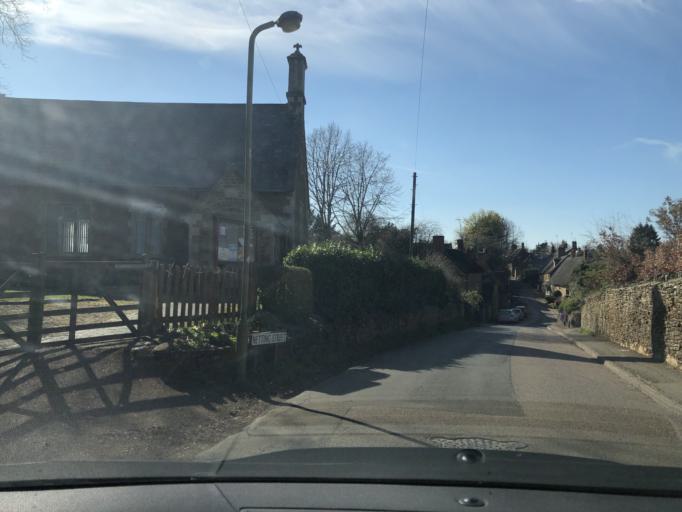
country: GB
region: England
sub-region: Oxfordshire
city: Hook Norton
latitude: 51.9953
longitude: -1.4861
